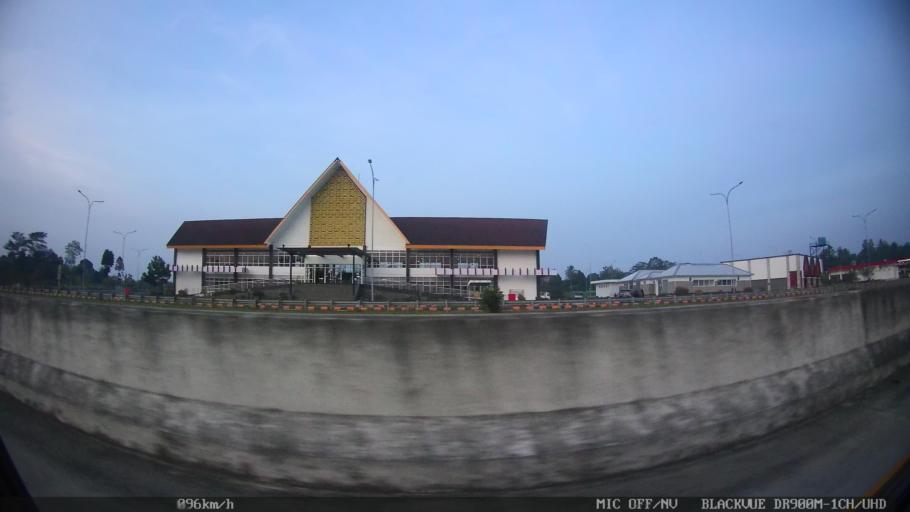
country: ID
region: Lampung
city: Pasuruan
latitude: -5.7262
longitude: 105.6682
